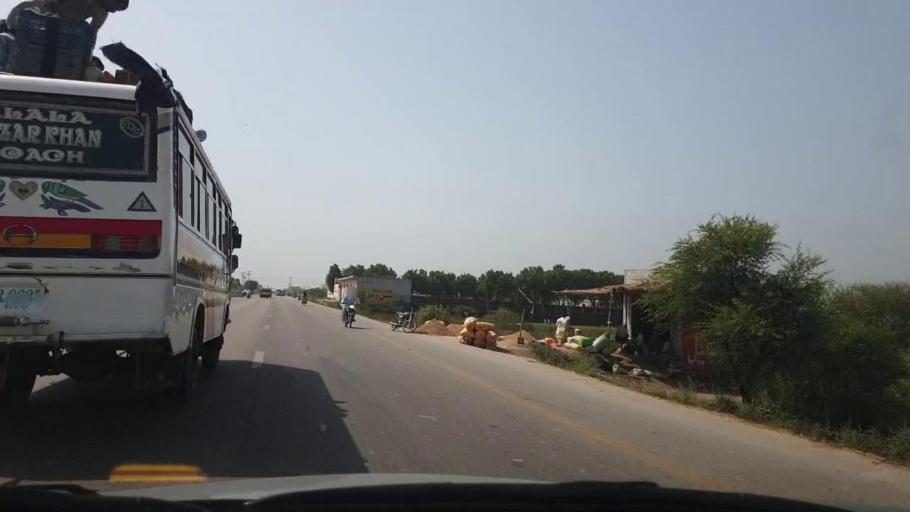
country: PK
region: Sindh
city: Matli
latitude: 25.0296
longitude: 68.6534
